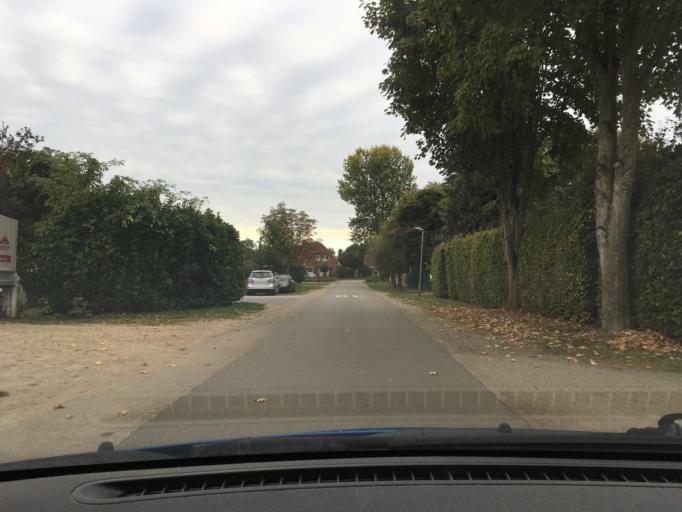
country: DE
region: Lower Saxony
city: Winsen
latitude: 53.3523
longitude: 10.2389
